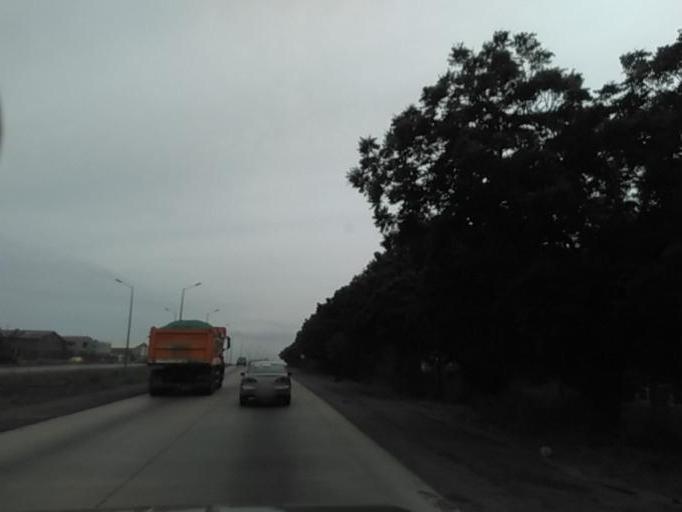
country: GH
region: Greater Accra
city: Medina Estates
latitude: 5.6325
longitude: -0.1496
